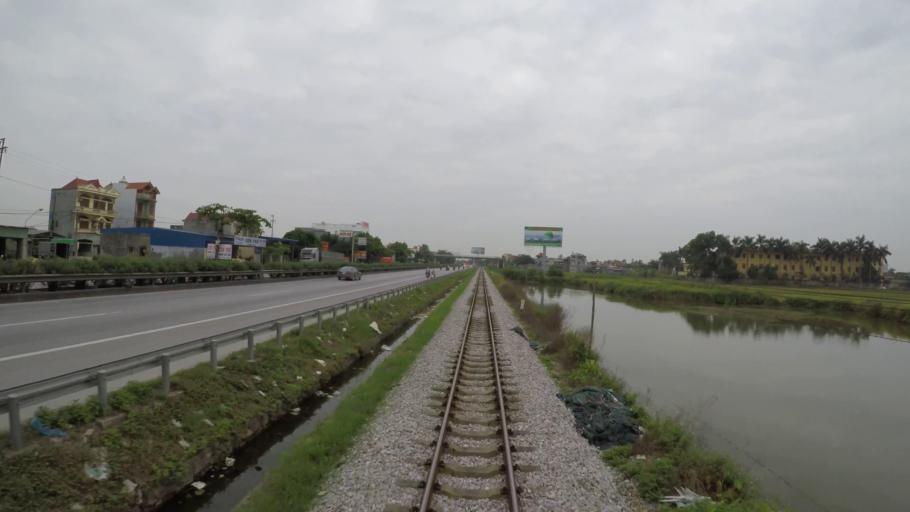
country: VN
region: Hai Duong
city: Phu Thai
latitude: 20.9233
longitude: 106.5586
